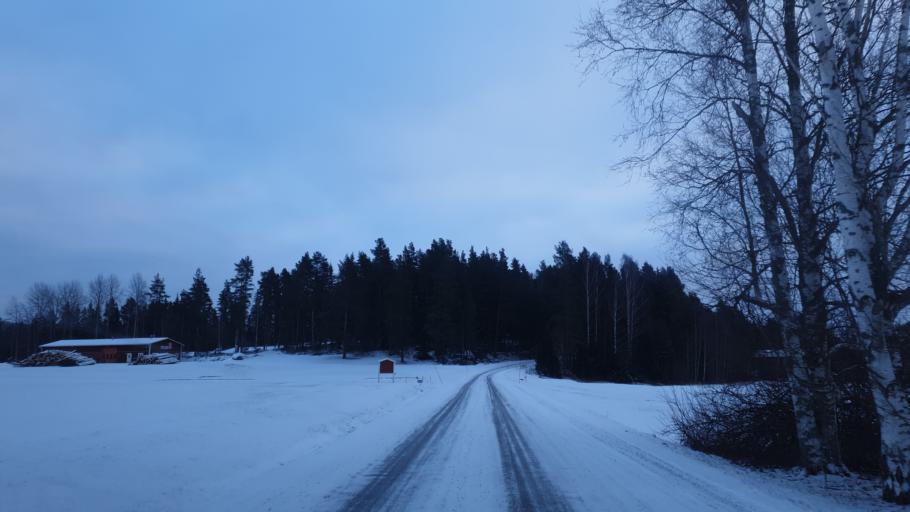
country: SE
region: Gaevleborg
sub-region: Bollnas Kommun
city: Kilafors
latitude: 61.2560
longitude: 16.5387
